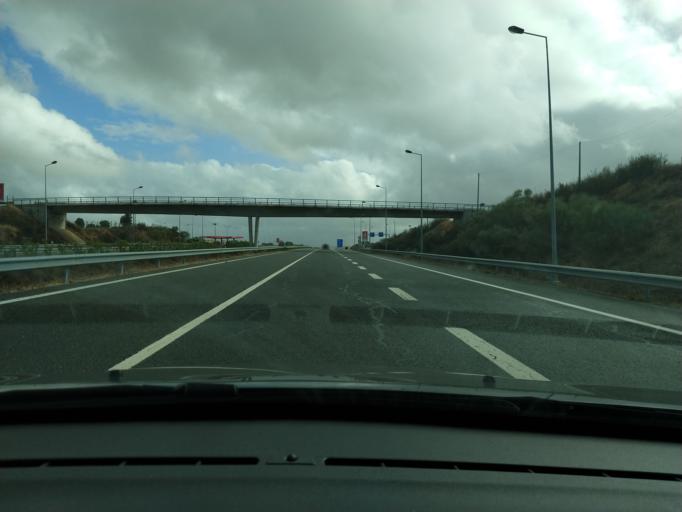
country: PT
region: Beja
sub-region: Ourique
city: Ourique
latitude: 37.5391
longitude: -8.1853
